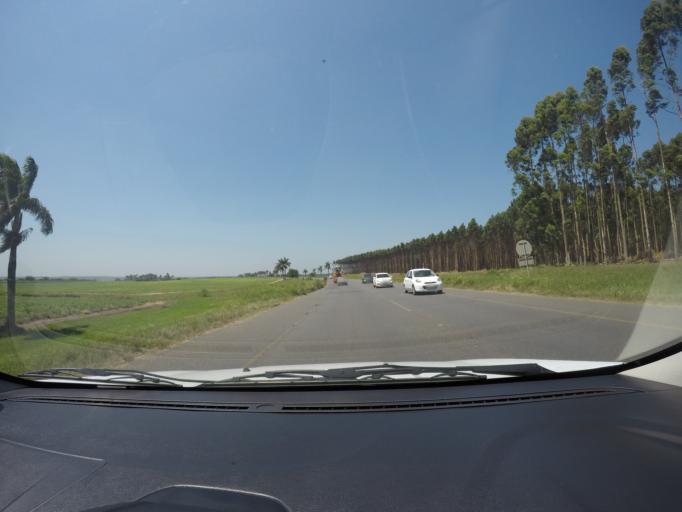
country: ZA
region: KwaZulu-Natal
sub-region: uThungulu District Municipality
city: eSikhawini
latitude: -28.8170
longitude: 31.9532
